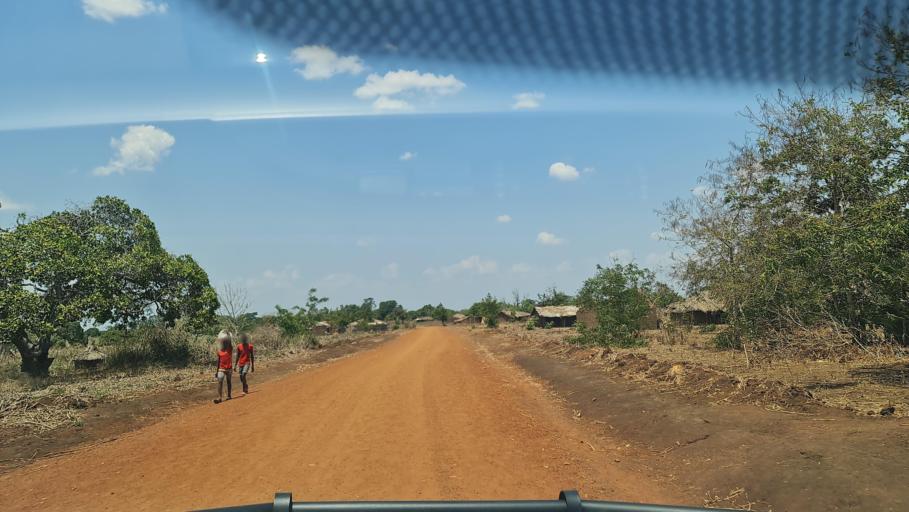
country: MZ
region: Nampula
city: Nacala
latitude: -14.8024
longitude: 40.0707
